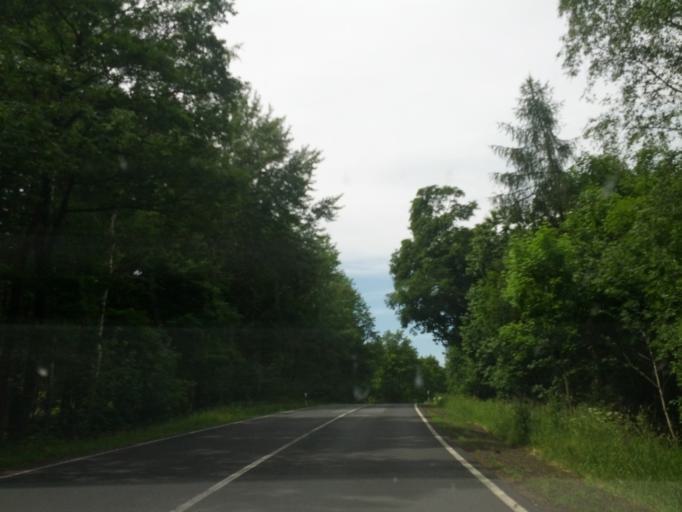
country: DE
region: Thuringia
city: Tabarz
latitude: 50.8698
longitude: 10.5341
